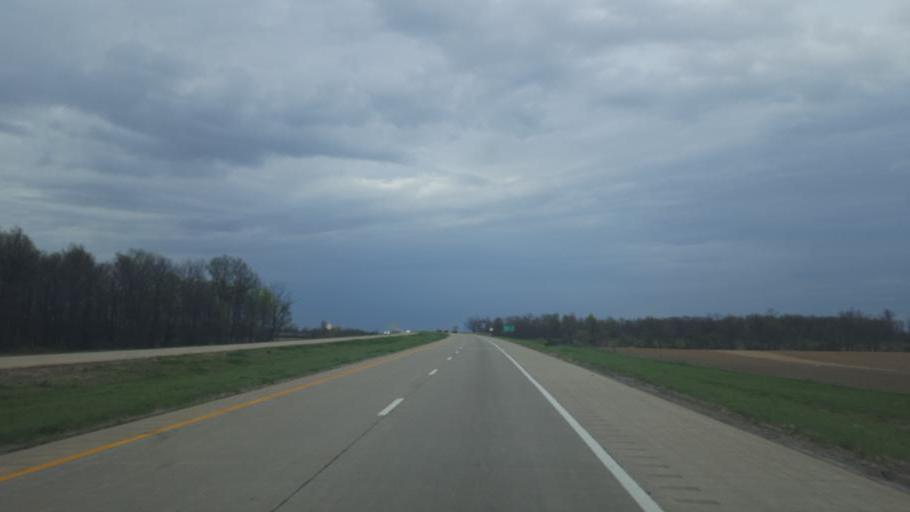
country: US
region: Ohio
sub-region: Crawford County
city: Bucyrus
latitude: 40.8102
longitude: -83.1097
